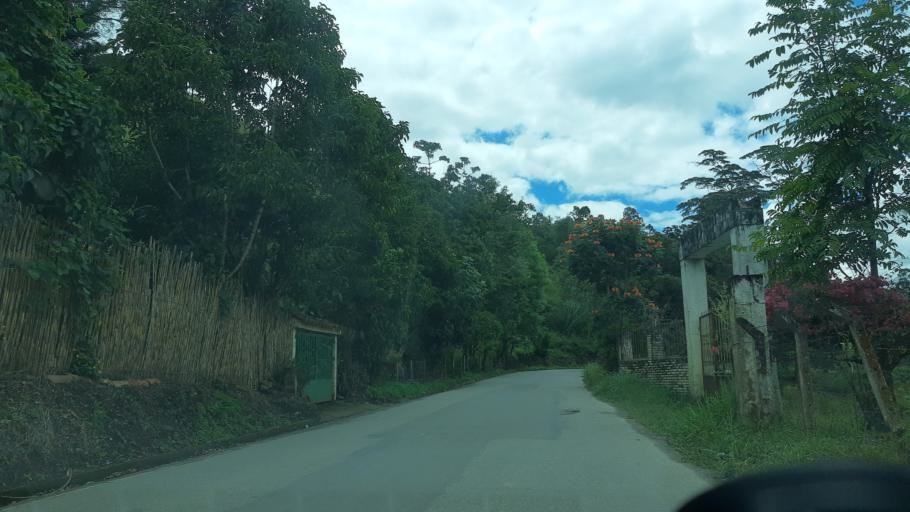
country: CO
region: Boyaca
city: Garagoa
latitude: 5.0650
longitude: -73.3822
